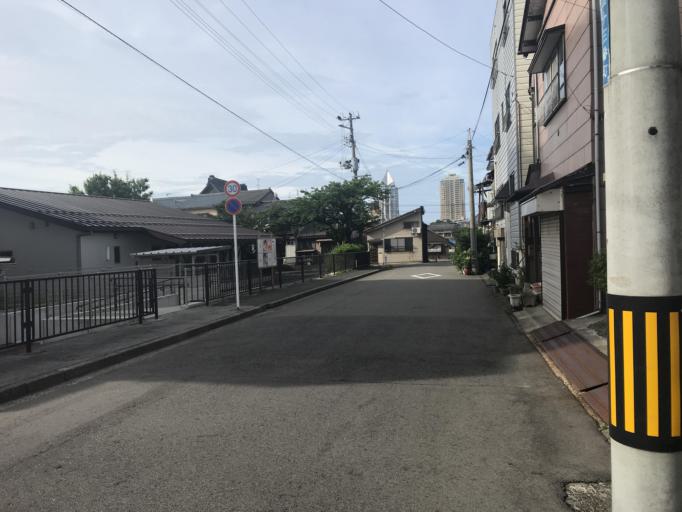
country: JP
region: Niigata
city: Niigata-shi
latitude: 37.9309
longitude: 139.0450
